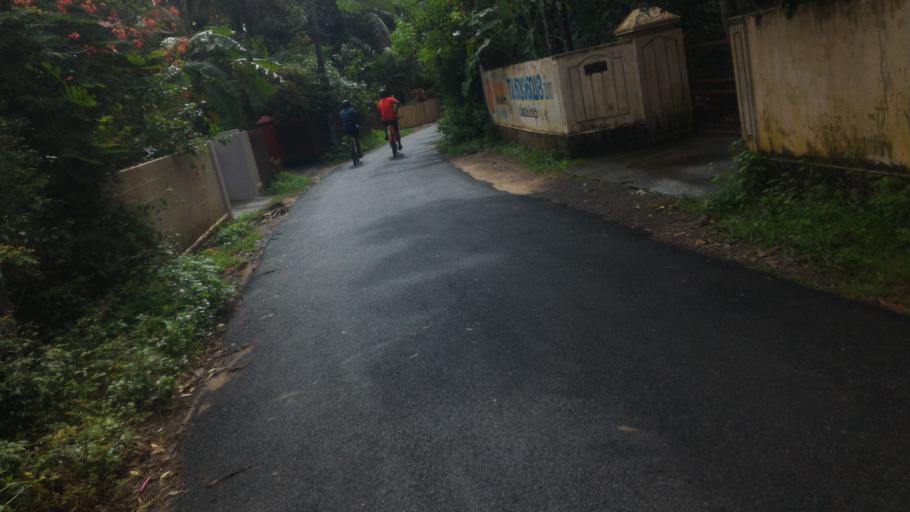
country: IN
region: Kerala
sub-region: Thrissur District
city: Thanniyam
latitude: 10.4221
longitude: 76.1081
